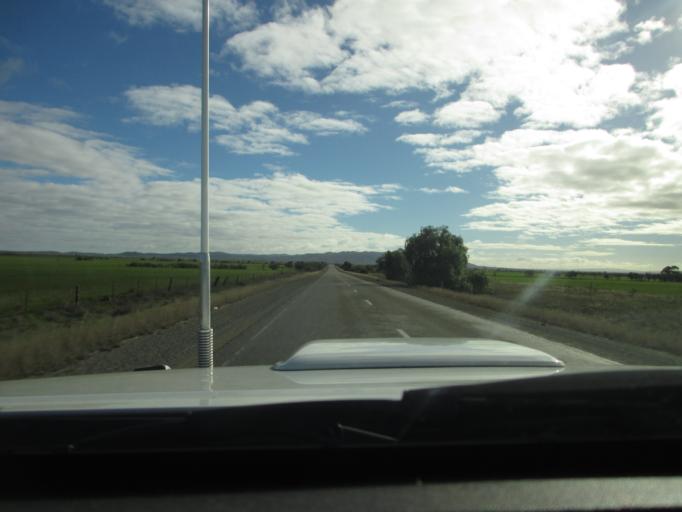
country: AU
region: South Australia
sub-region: Peterborough
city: Peterborough
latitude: -32.6804
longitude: 138.6083
